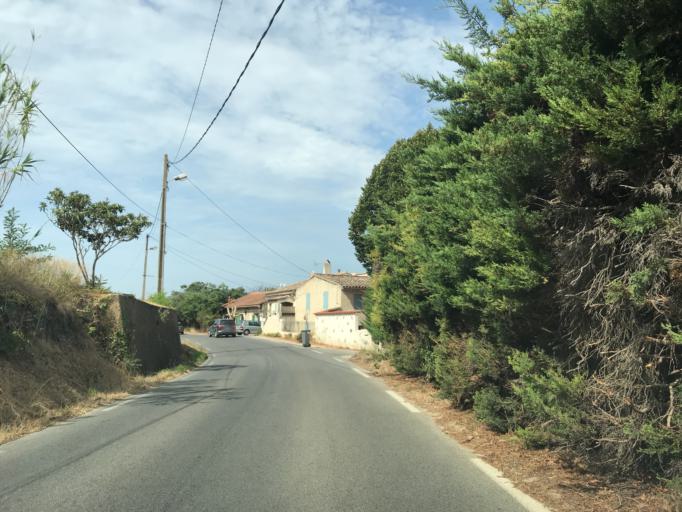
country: FR
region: Provence-Alpes-Cote d'Azur
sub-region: Departement du Var
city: Saint-Cyr-sur-Mer
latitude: 43.1739
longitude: 5.7262
